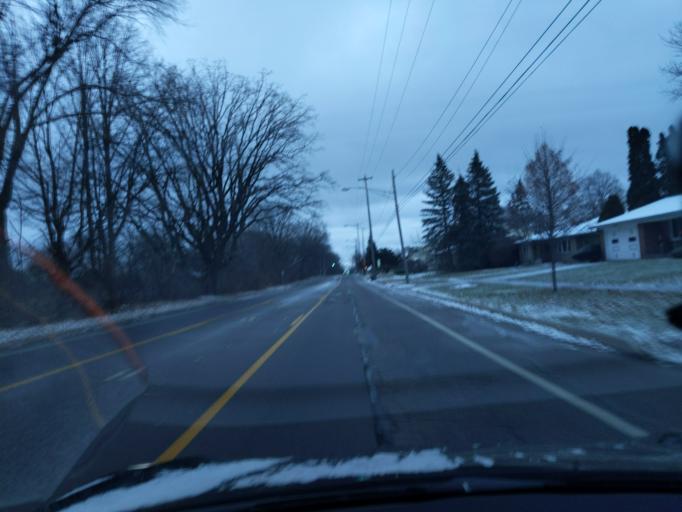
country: US
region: Michigan
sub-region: Ingham County
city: Edgemont Park
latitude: 42.7121
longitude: -84.5856
